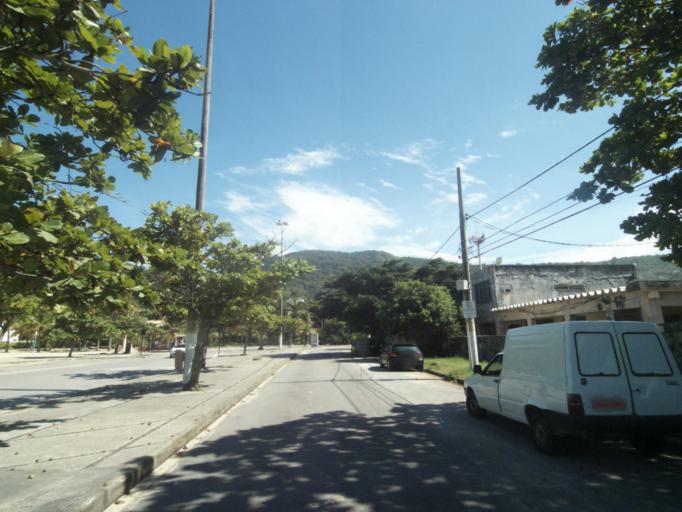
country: BR
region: Rio de Janeiro
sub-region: Niteroi
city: Niteroi
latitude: -22.9528
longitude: -43.0973
